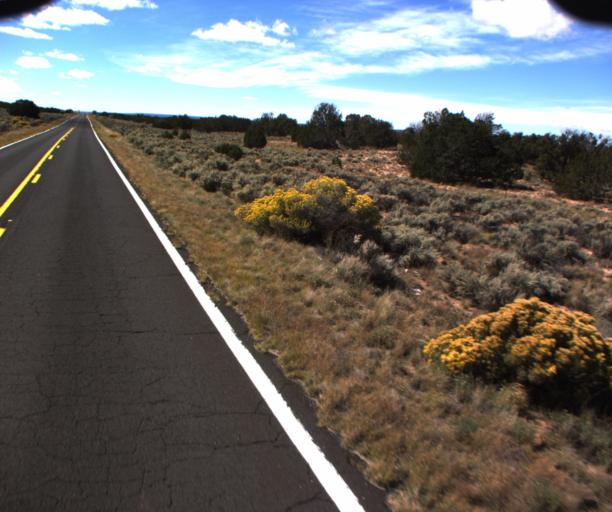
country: US
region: Arizona
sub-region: Apache County
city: Houck
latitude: 34.9080
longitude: -109.2283
